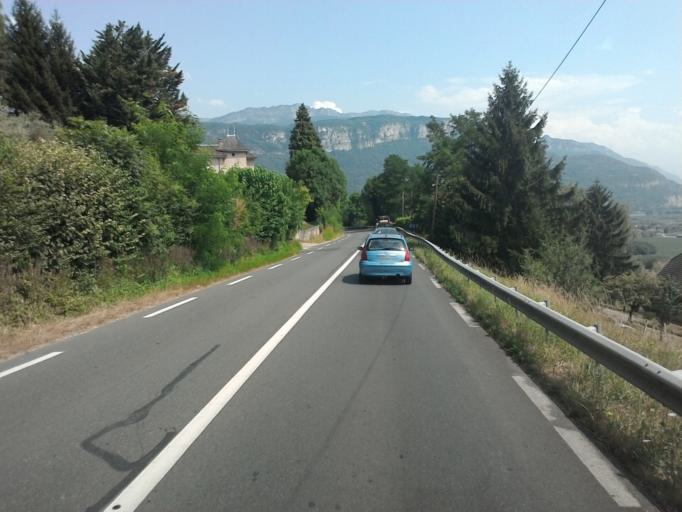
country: FR
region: Rhone-Alpes
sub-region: Departement de l'Isere
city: Saint-Jean-de-Moirans
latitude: 45.3467
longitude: 5.5961
